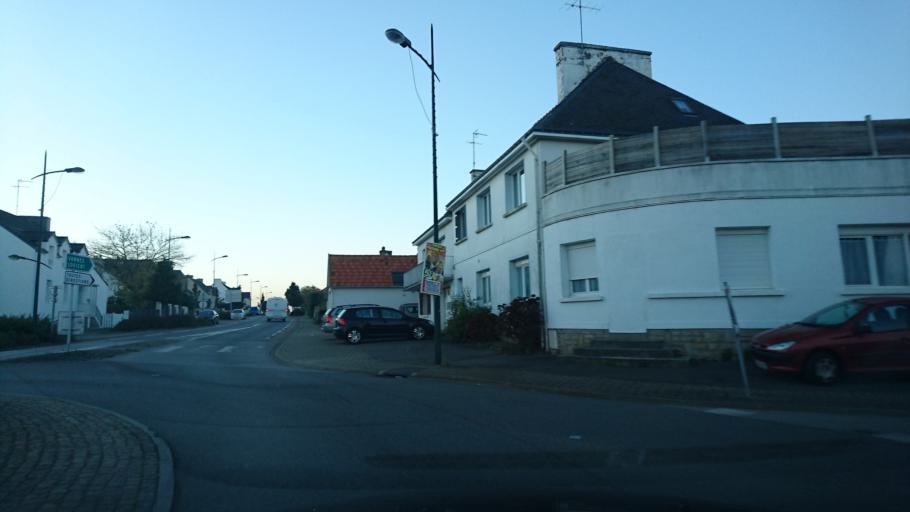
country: FR
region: Brittany
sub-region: Departement du Morbihan
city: Auray
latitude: 47.6781
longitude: -3.0090
